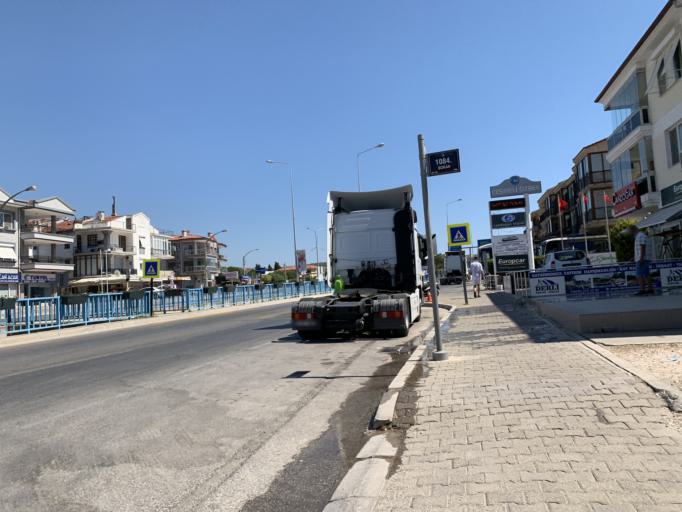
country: TR
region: Izmir
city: Cesme
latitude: 38.3171
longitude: 26.3036
